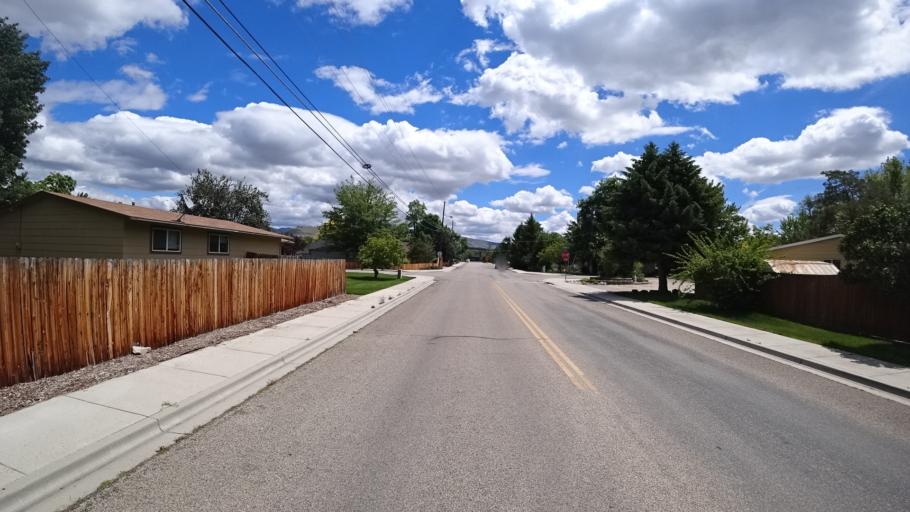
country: US
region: Idaho
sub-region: Ada County
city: Boise
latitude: 43.5844
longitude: -116.1878
